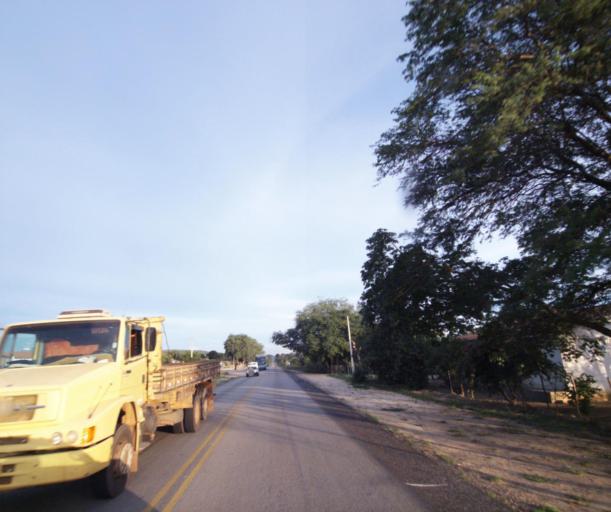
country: BR
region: Bahia
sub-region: Brumado
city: Brumado
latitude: -14.2335
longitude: -41.8993
